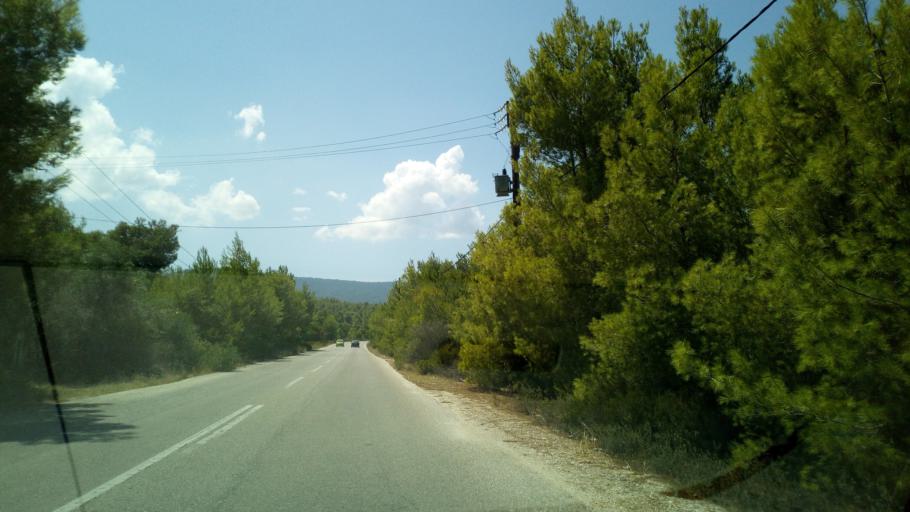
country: GR
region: Central Macedonia
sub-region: Nomos Chalkidikis
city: Sarti
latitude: 40.1262
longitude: 23.9595
